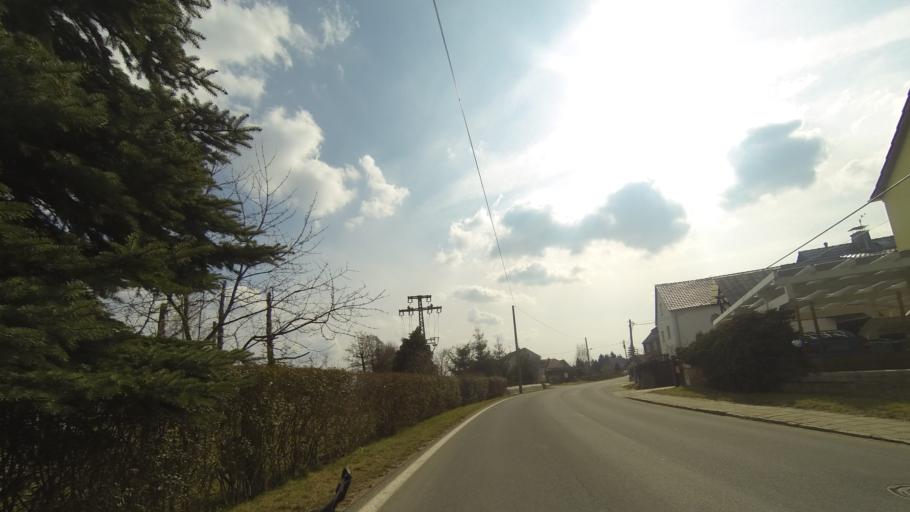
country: DE
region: Saxony
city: Moritzburg
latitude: 51.1619
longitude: 13.7319
